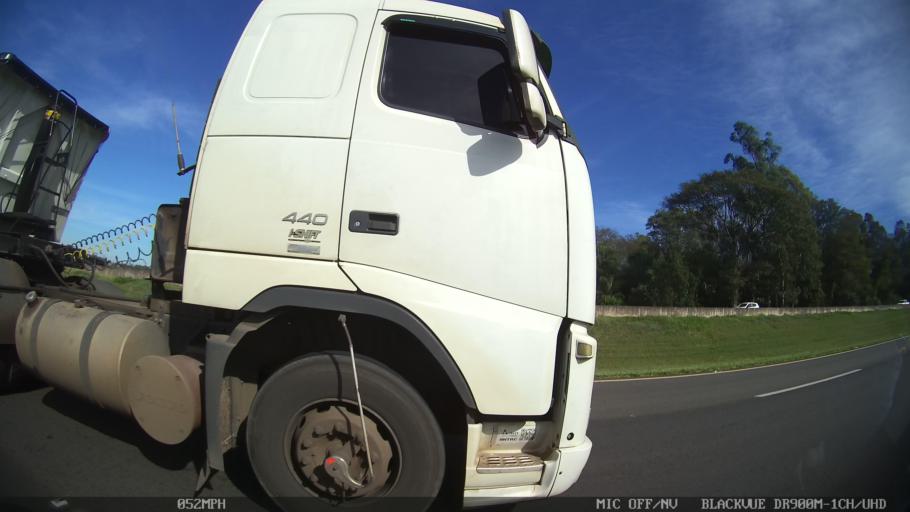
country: BR
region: Sao Paulo
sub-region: Araras
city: Araras
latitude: -22.3926
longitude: -47.3923
